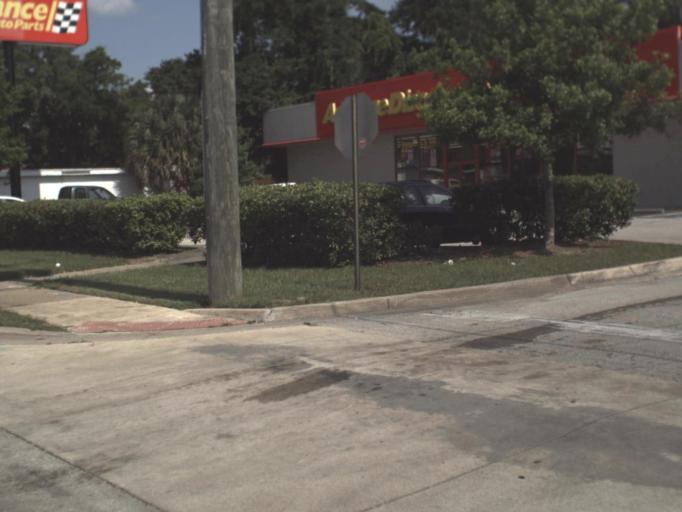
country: US
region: Florida
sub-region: Duval County
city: Jacksonville
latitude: 30.2905
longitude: -81.5938
